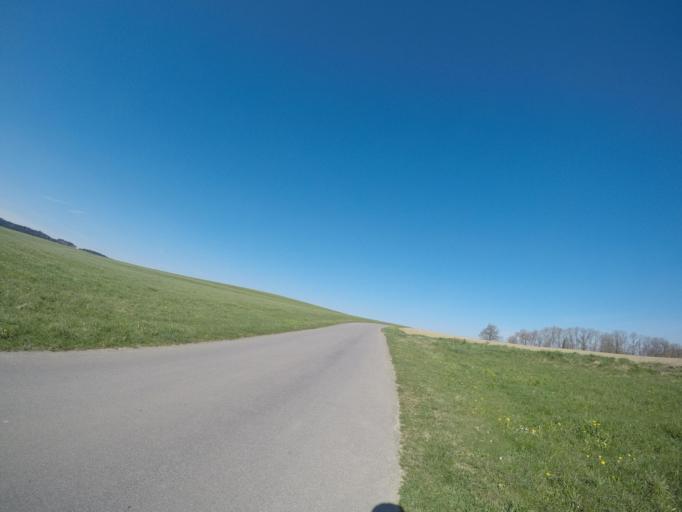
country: DE
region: Baden-Wuerttemberg
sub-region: Tuebingen Region
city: Fleischwangen
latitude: 47.8716
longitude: 9.5069
